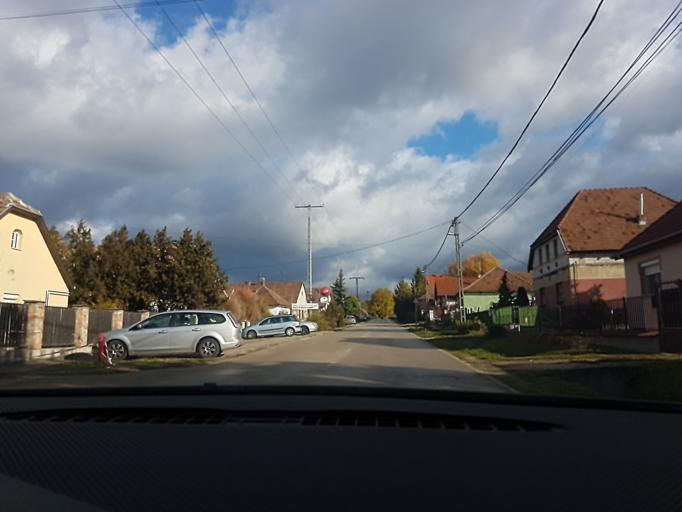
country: HU
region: Pest
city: Szada
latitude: 47.6324
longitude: 19.3050
